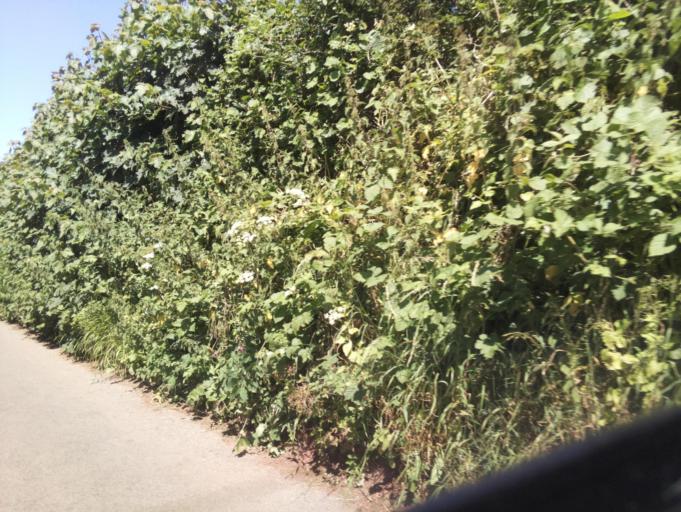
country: GB
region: England
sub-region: Devon
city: Marldon
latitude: 50.4658
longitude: -3.5961
